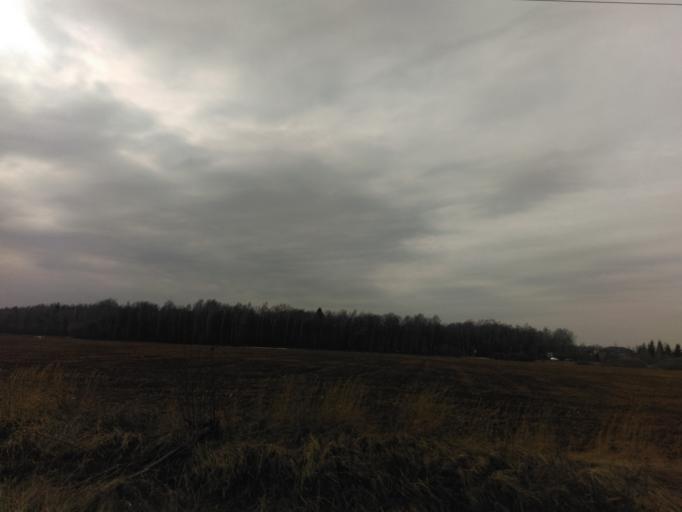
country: RU
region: Moskovskaya
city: Yershovo
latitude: 55.7533
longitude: 36.9376
